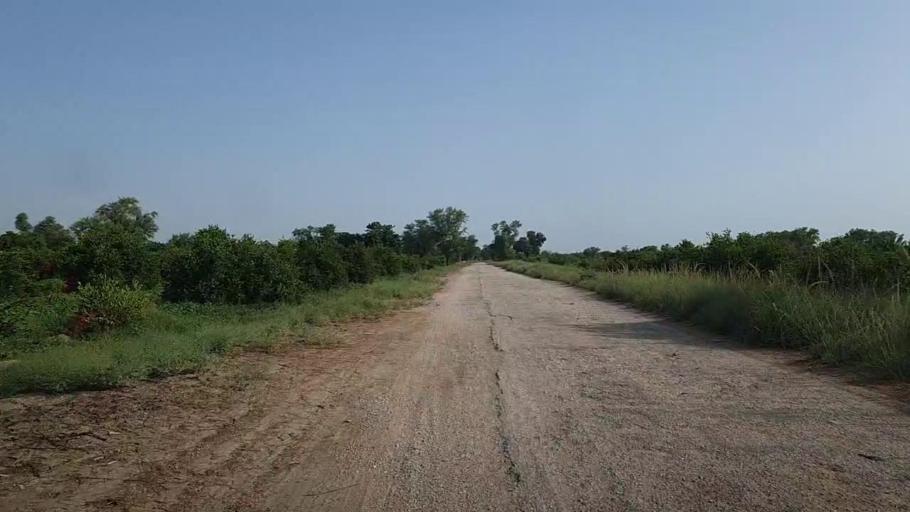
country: PK
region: Sindh
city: Karaundi
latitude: 26.8606
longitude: 68.3309
